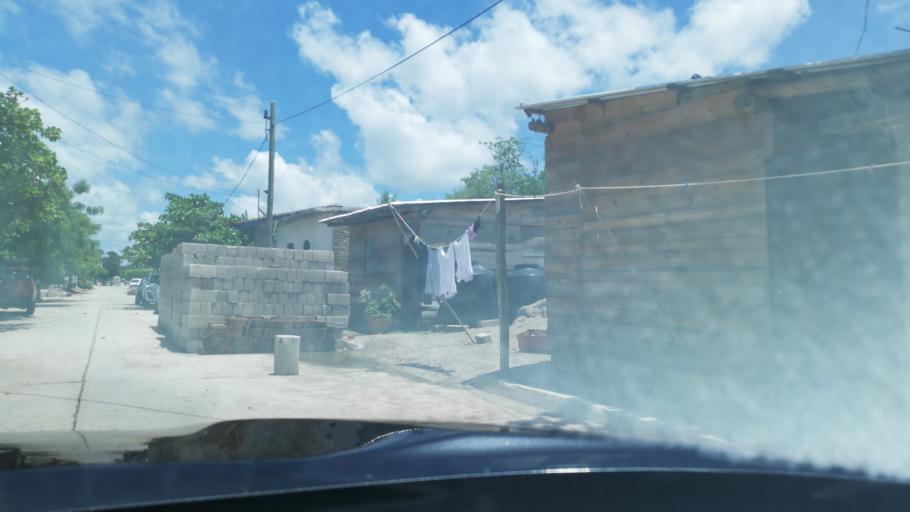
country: MX
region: Oaxaca
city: Asuncion Ixtaltepec
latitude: 16.5069
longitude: -95.0570
